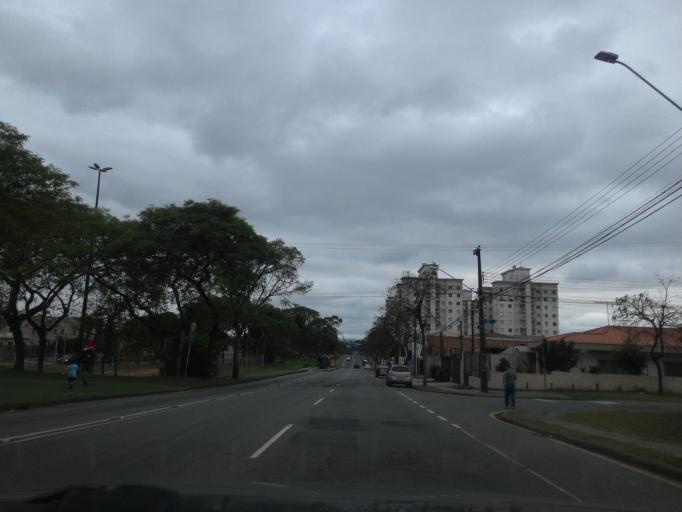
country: BR
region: Parana
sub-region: Curitiba
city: Curitiba
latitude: -25.4754
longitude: -49.2753
